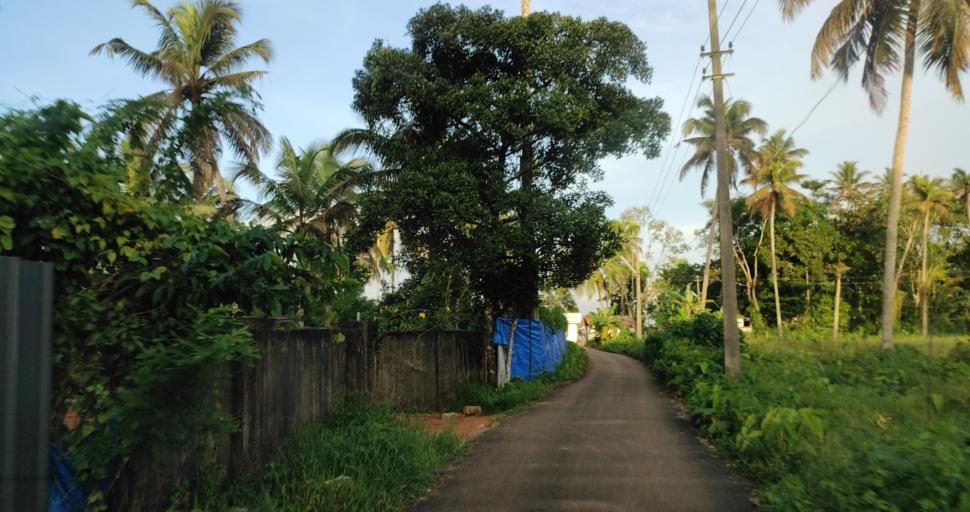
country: IN
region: Kerala
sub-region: Alappuzha
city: Shertallai
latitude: 9.6037
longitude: 76.3645
